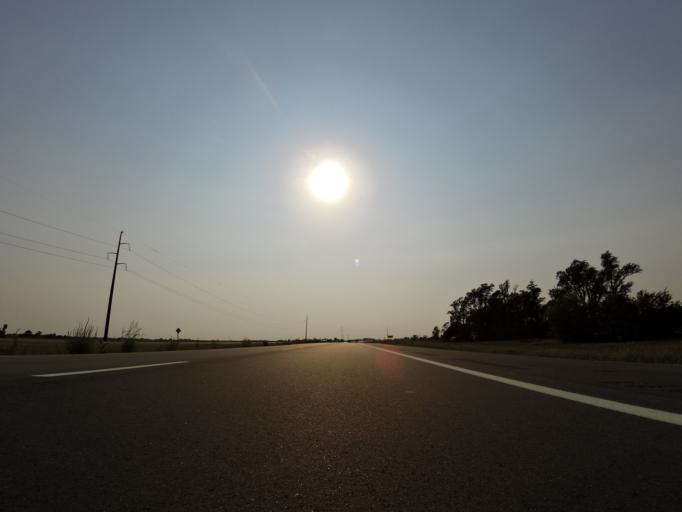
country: US
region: Kansas
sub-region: Reno County
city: South Hutchinson
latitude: 38.0135
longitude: -97.9695
